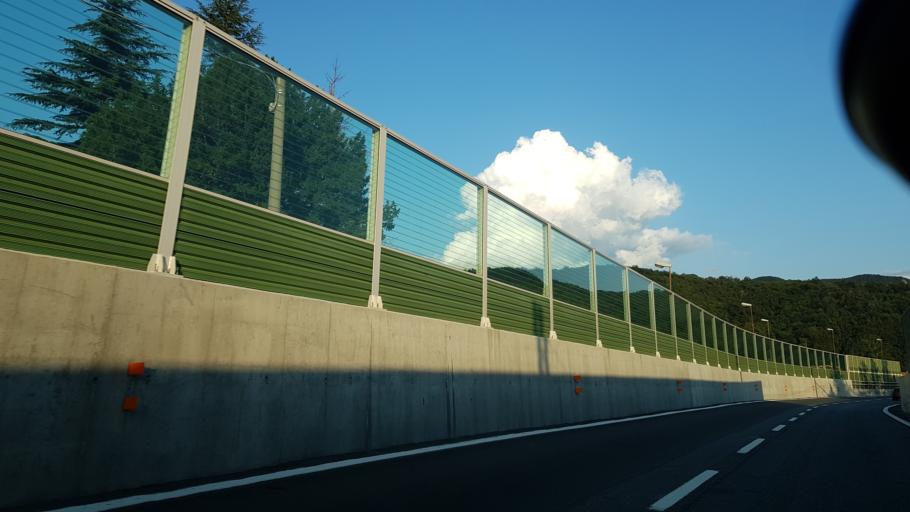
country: IT
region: Liguria
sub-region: Provincia di Genova
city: Ronco Scrivia
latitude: 44.6146
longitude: 8.9533
